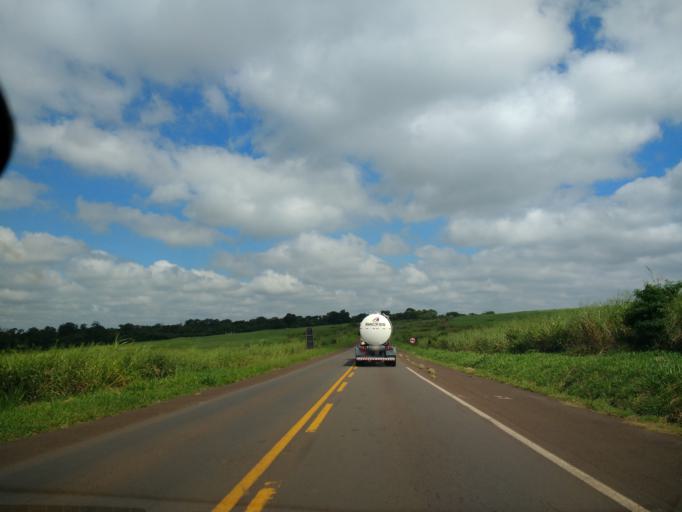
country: BR
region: Parana
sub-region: Cruzeiro Do Oeste
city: Cruzeiro do Oeste
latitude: -23.7686
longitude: -53.0111
